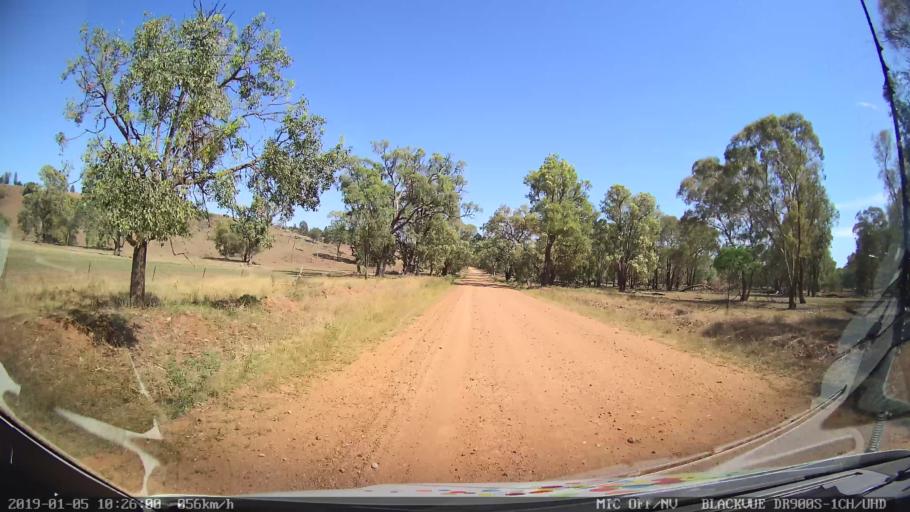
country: AU
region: New South Wales
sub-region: Gilgandra
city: Gilgandra
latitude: -31.5569
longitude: 148.9568
